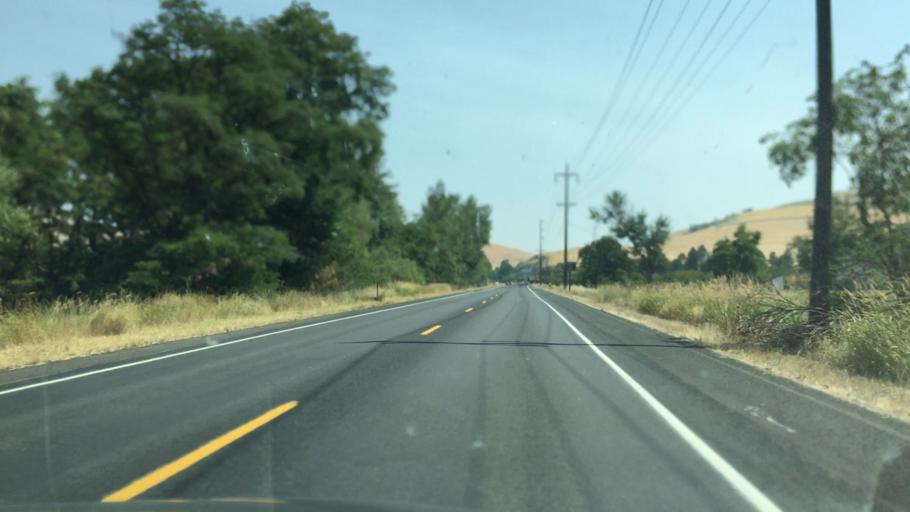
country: US
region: Idaho
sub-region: Nez Perce County
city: Lapwai
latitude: 46.3680
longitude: -116.7321
